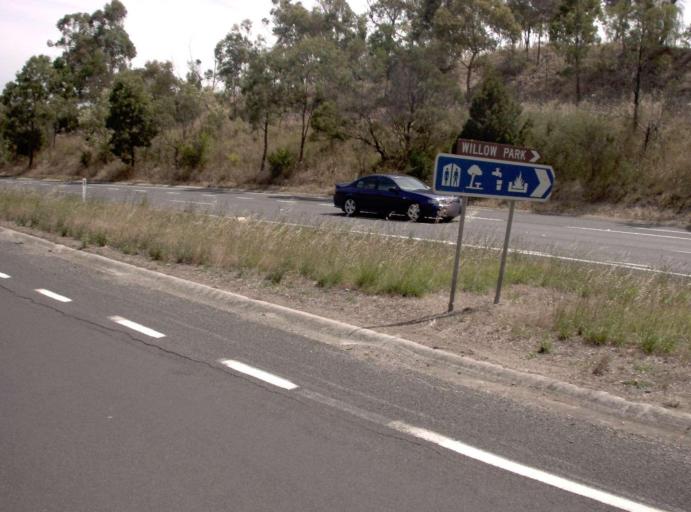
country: AU
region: Victoria
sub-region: Wellington
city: Heyfield
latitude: -38.1391
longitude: 146.7939
